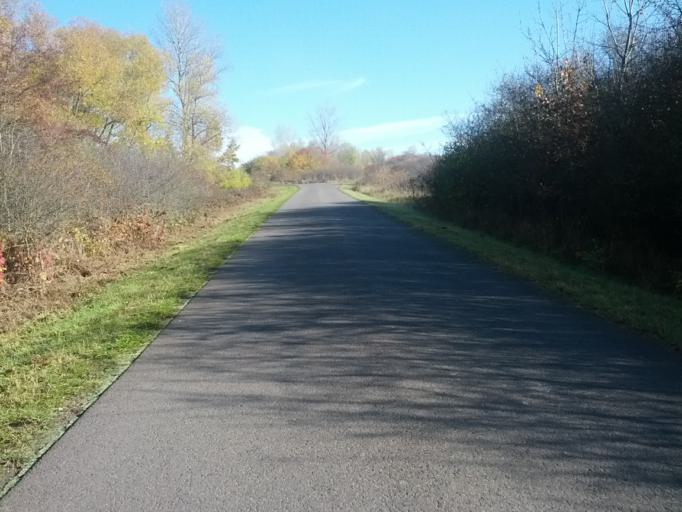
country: DE
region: Thuringia
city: Haina
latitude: 50.9980
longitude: 10.4369
